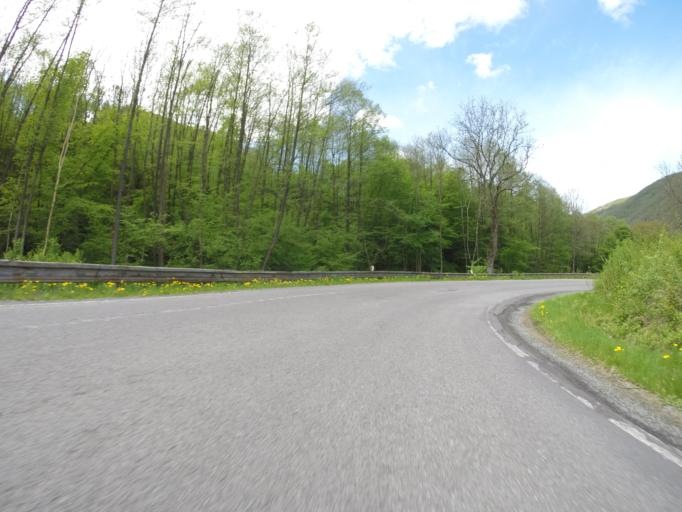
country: SK
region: Banskobystricky
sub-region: Okres Banska Bystrica
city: Zvolen
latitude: 48.5593
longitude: 19.0488
